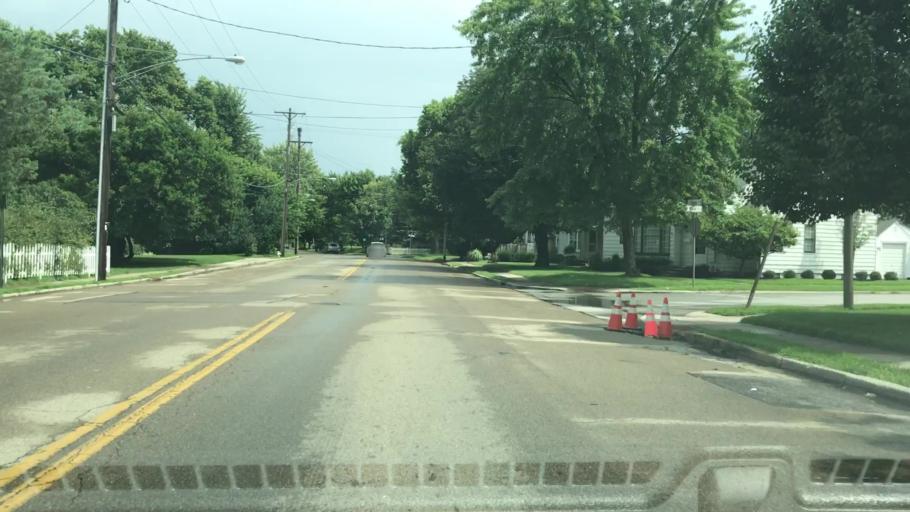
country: US
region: Ohio
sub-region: Greene County
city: Fairborn
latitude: 39.8249
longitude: -84.0247
